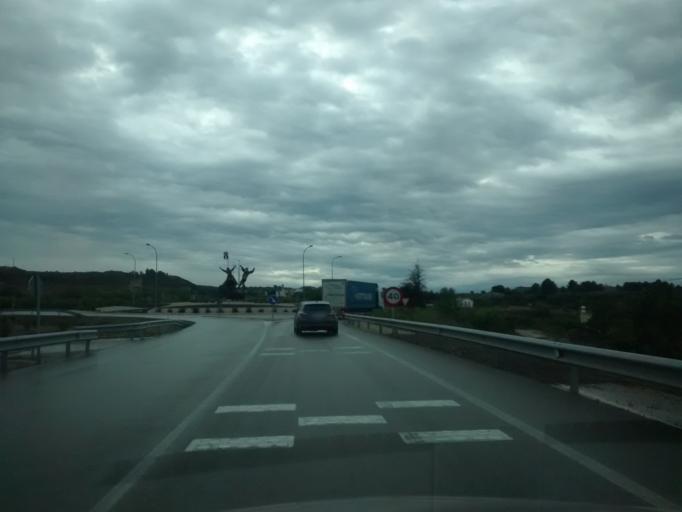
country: ES
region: Aragon
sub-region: Provincia de Zaragoza
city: Maella
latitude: 41.1287
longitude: 0.1307
